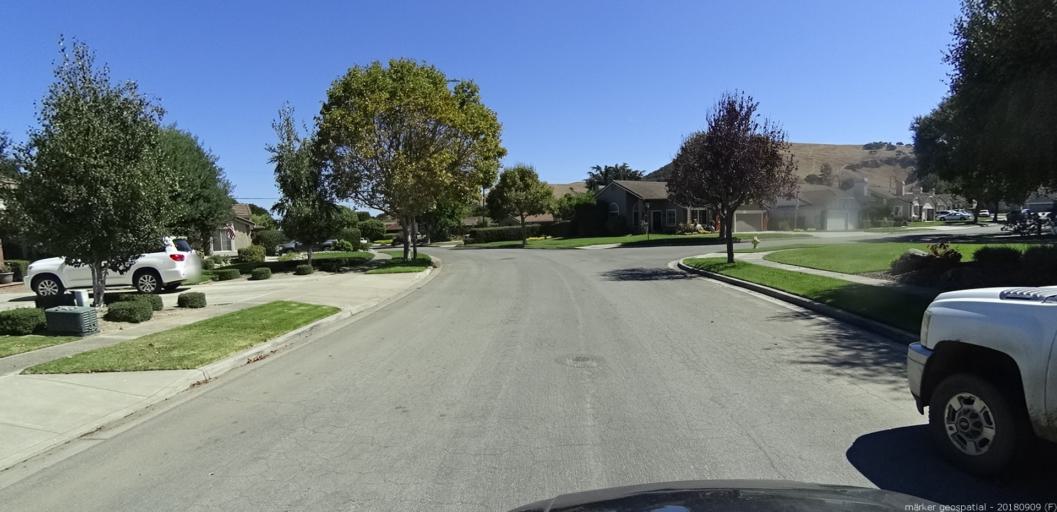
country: US
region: California
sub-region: Monterey County
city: Salinas
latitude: 36.6087
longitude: -121.6956
